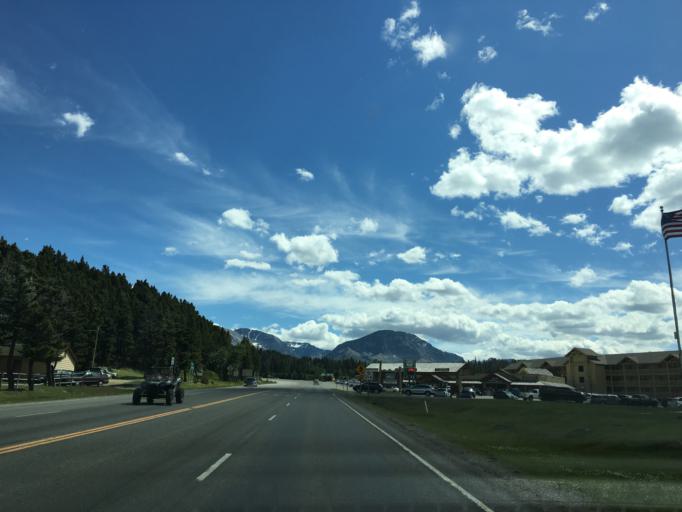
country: US
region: Montana
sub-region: Glacier County
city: North Browning
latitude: 48.7445
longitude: -113.4292
